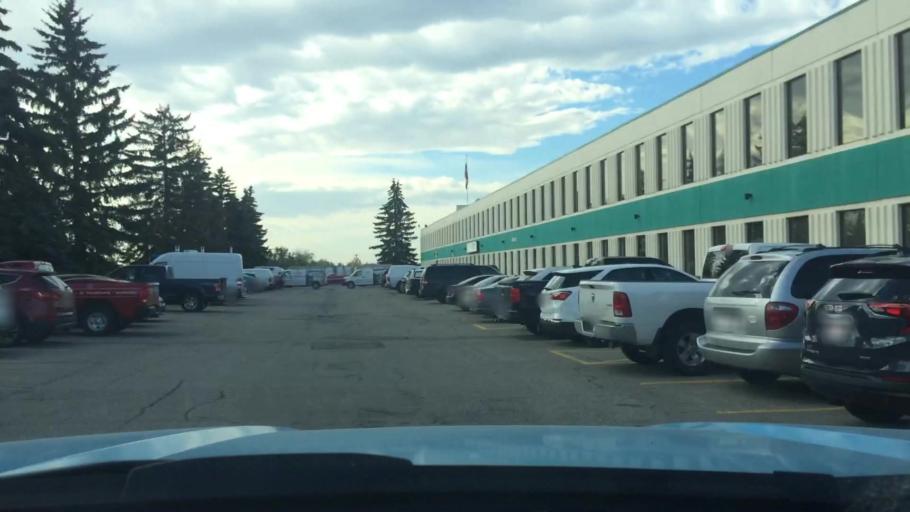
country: CA
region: Alberta
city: Calgary
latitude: 50.9948
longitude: -113.9768
